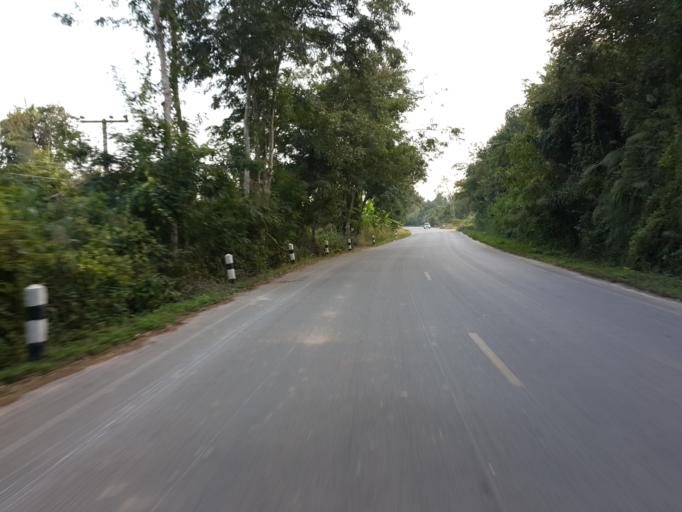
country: TH
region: Lamphun
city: Thung Hua Chang
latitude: 17.9760
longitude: 99.0414
